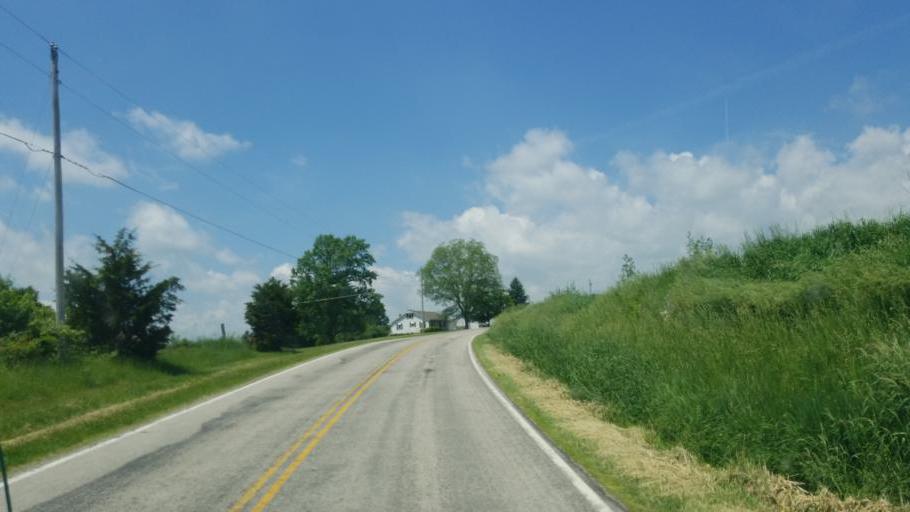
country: US
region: Ohio
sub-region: Ashland County
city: Ashland
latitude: 40.8188
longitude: -82.2602
